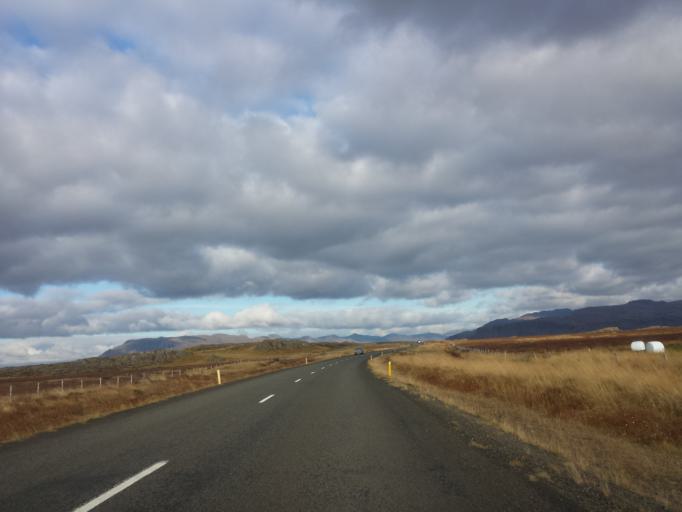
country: IS
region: West
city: Borgarnes
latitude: 64.6694
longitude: -22.0706
